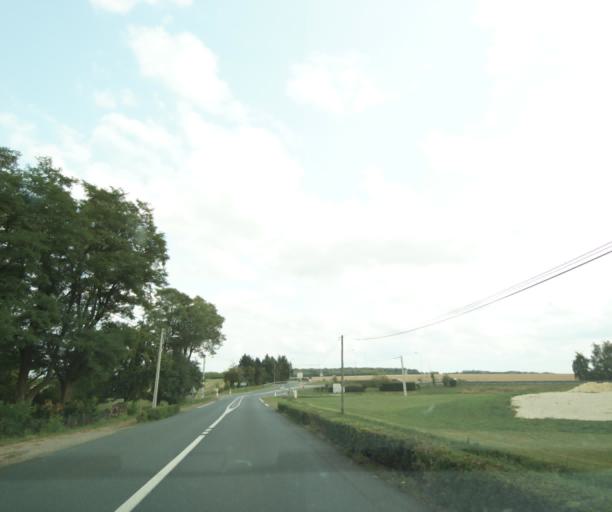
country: FR
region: Centre
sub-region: Departement de l'Indre
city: Buzancais
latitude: 46.8819
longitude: 1.4498
